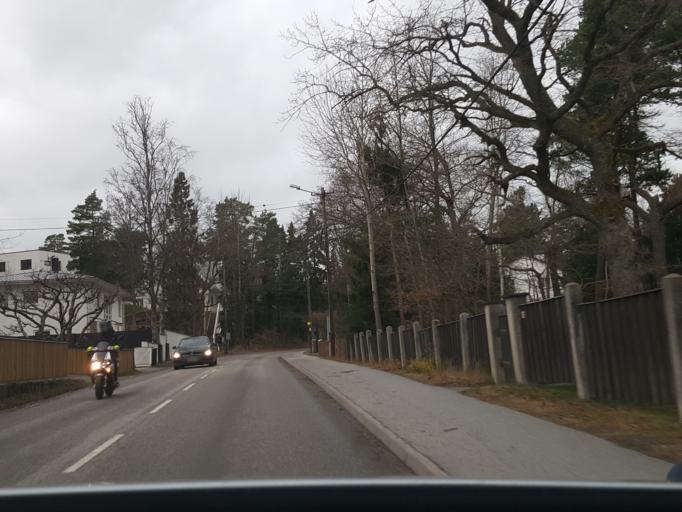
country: SE
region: Stockholm
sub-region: Nacka Kommun
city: Boo
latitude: 59.3254
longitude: 18.2891
